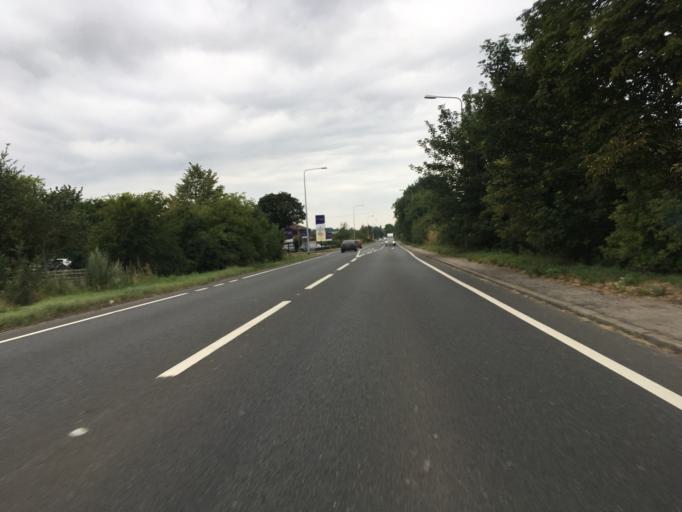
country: GB
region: England
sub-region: Central Bedfordshire
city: Hockliffe
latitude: 51.9210
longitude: -0.5712
